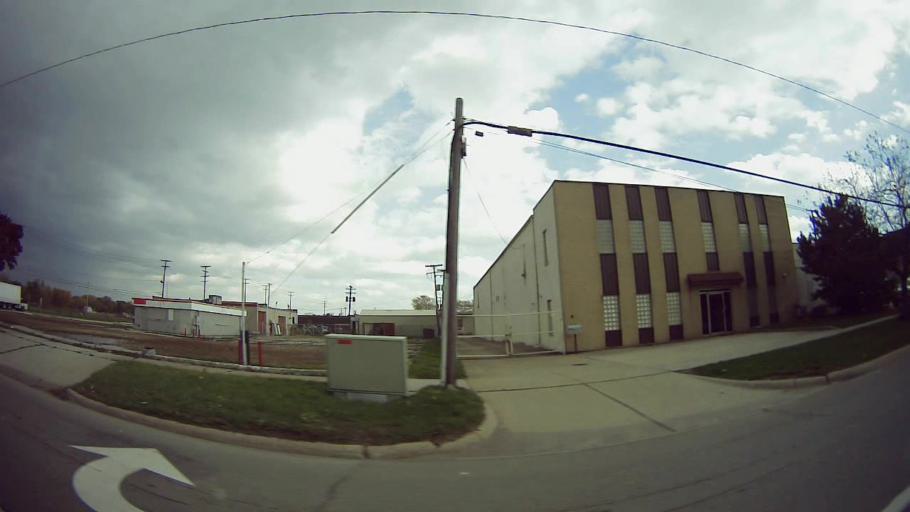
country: US
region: Michigan
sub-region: Macomb County
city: Warren
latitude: 42.4629
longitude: -83.0055
